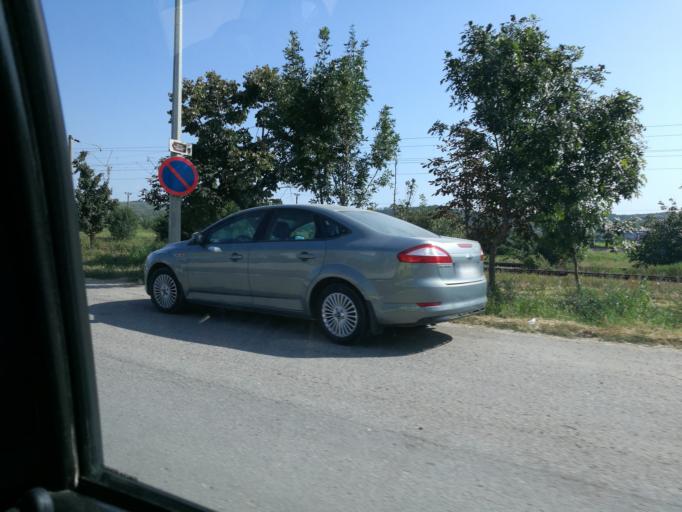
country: RO
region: Iasi
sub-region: Comuna Valea Lupului
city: Valea Lupului
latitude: 47.1725
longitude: 27.5156
